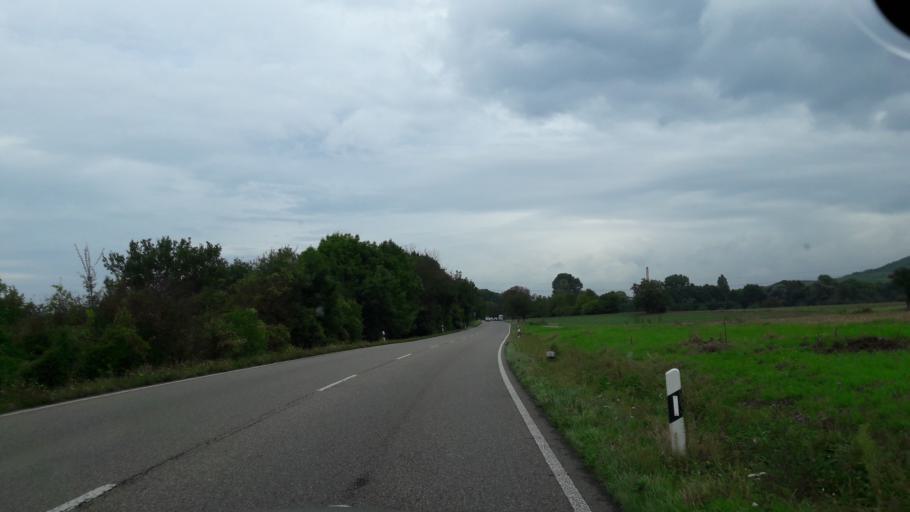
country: DE
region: Baden-Wuerttemberg
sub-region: Karlsruhe Region
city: Kronau
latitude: 49.2365
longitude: 8.6554
